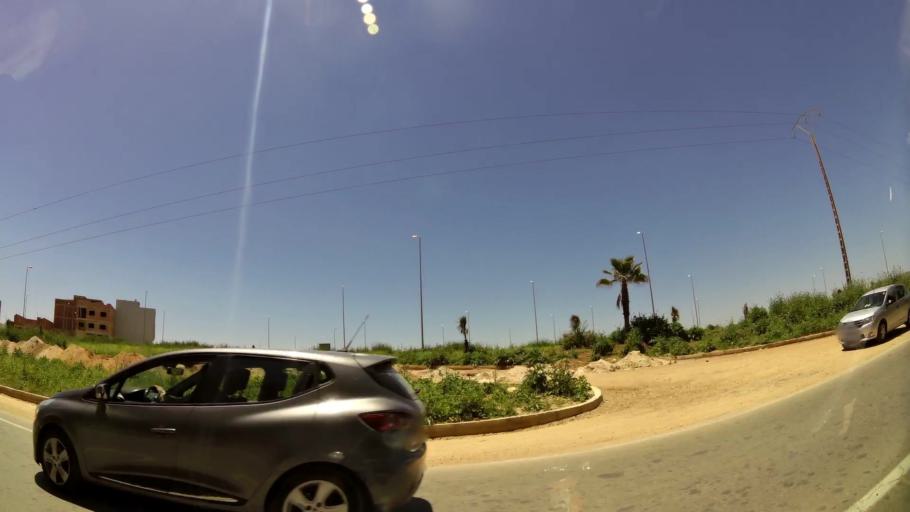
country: MA
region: Meknes-Tafilalet
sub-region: Meknes
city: Meknes
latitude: 33.8511
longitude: -5.5628
